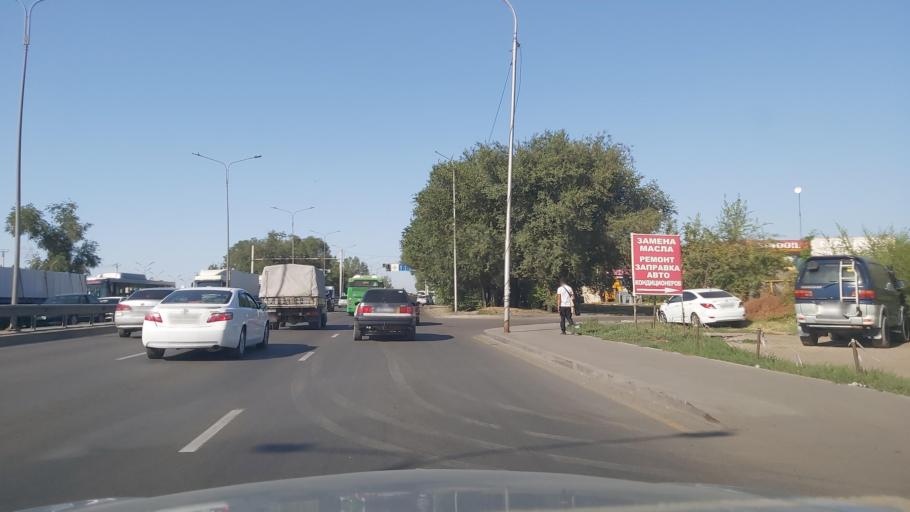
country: KZ
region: Almaty Oblysy
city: Pervomayskiy
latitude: 43.3239
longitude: 76.9068
